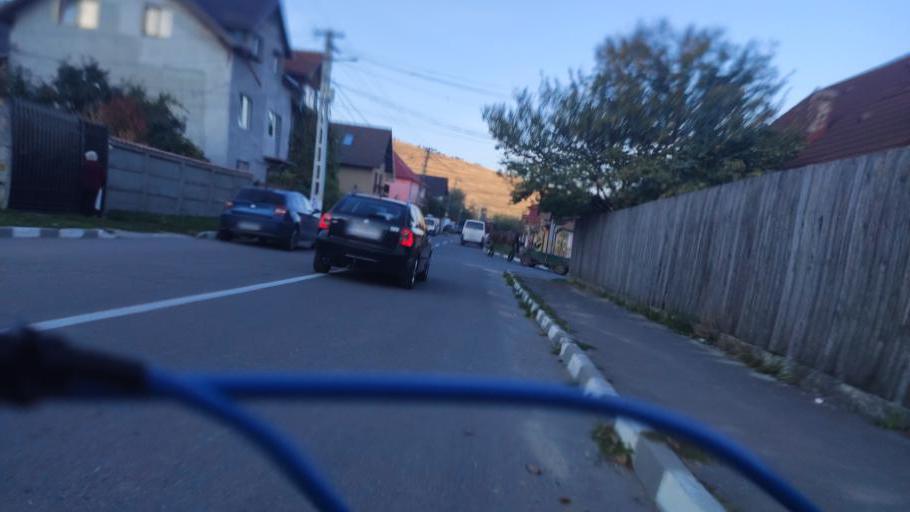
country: RO
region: Brasov
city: Codlea
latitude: 45.7056
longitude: 25.4436
